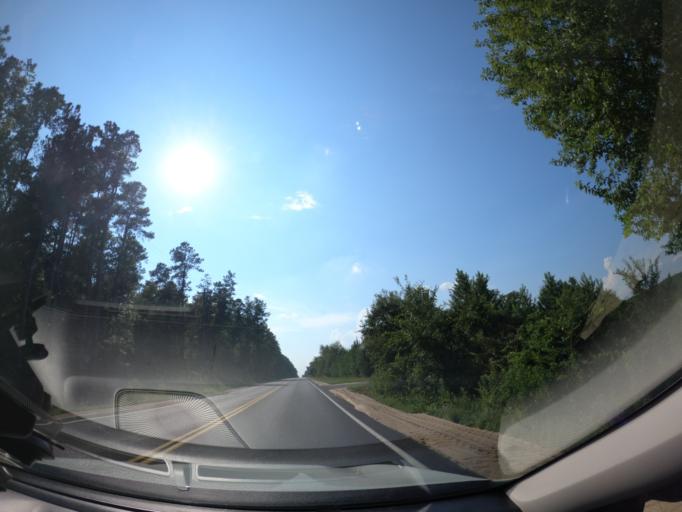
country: US
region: South Carolina
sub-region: Aiken County
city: New Ellenton
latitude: 33.3990
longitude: -81.7558
